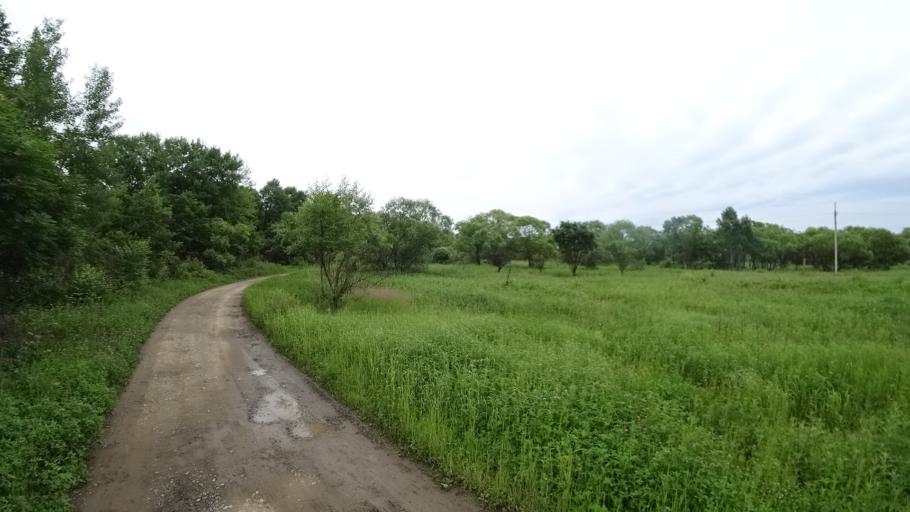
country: RU
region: Primorskiy
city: Novosysoyevka
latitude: 44.2090
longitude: 133.3276
